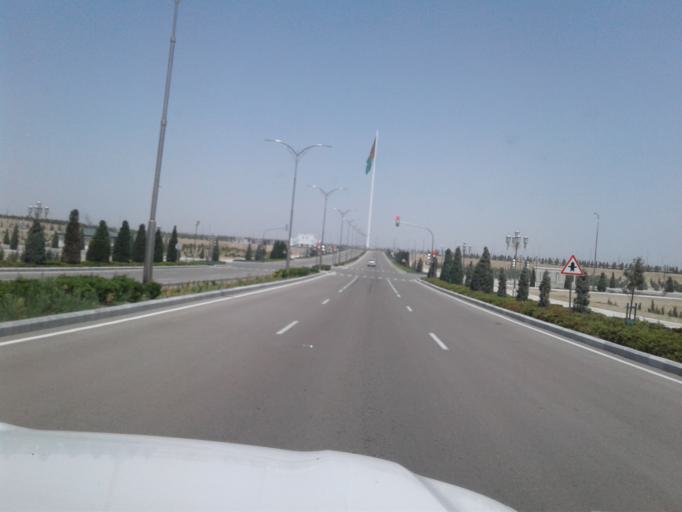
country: TM
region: Balkan
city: Turkmenbasy
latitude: 39.9561
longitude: 52.8598
